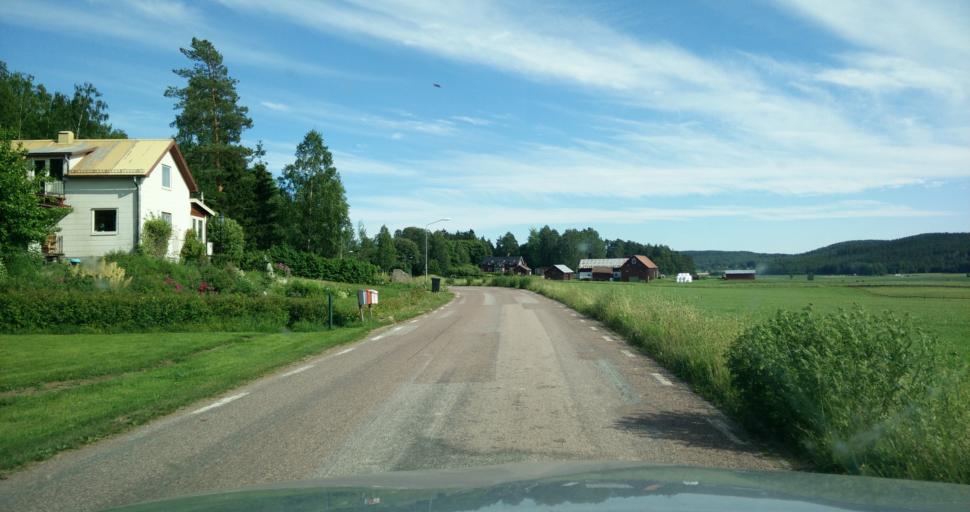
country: SE
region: Dalarna
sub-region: Hedemora Kommun
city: Langshyttan
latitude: 60.3866
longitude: 15.9841
